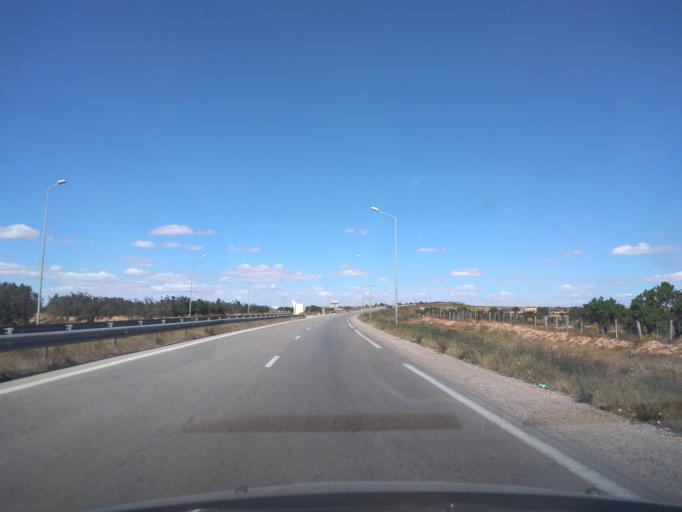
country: TN
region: Safaqis
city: Al Qarmadah
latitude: 34.8873
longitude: 10.7199
